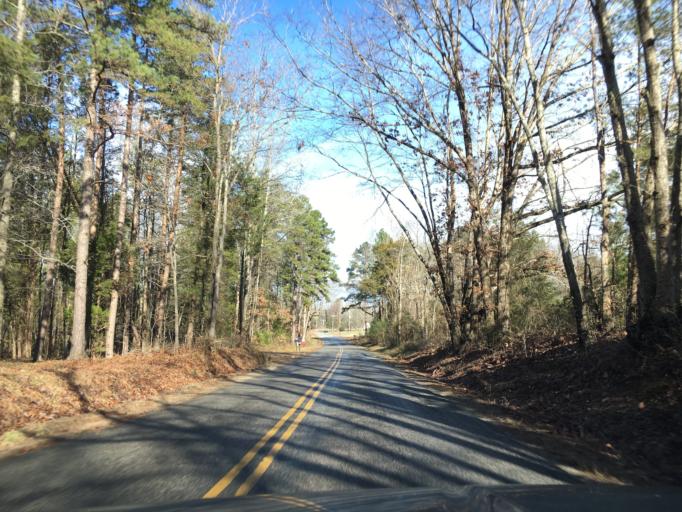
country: US
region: Virginia
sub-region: Nottoway County
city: Crewe
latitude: 37.3369
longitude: -78.1598
